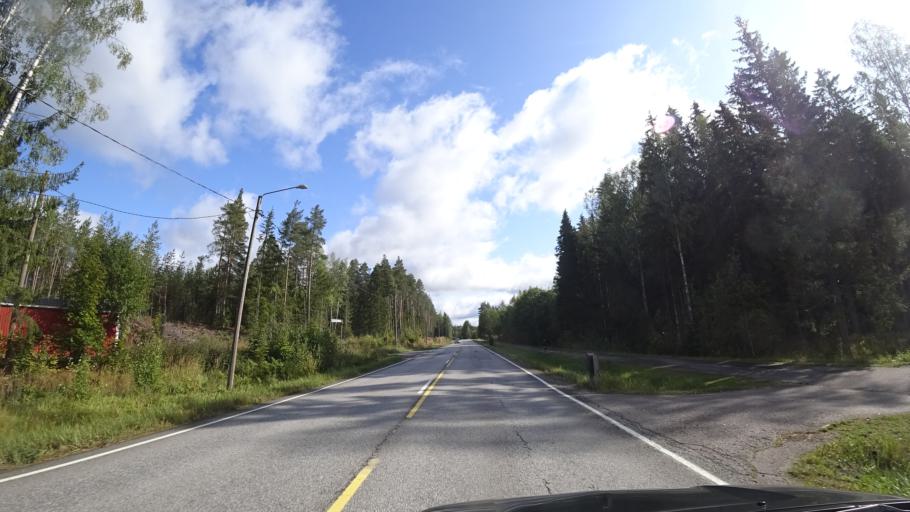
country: FI
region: Uusimaa
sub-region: Helsinki
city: Hyvinge
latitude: 60.5795
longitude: 24.9953
